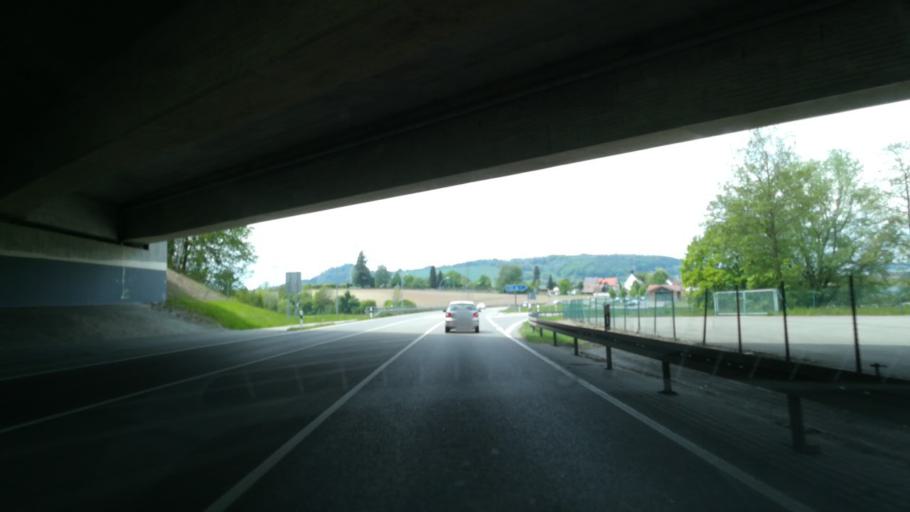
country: DE
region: Baden-Wuerttemberg
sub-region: Freiburg Region
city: Stockach
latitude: 47.8411
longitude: 9.0224
